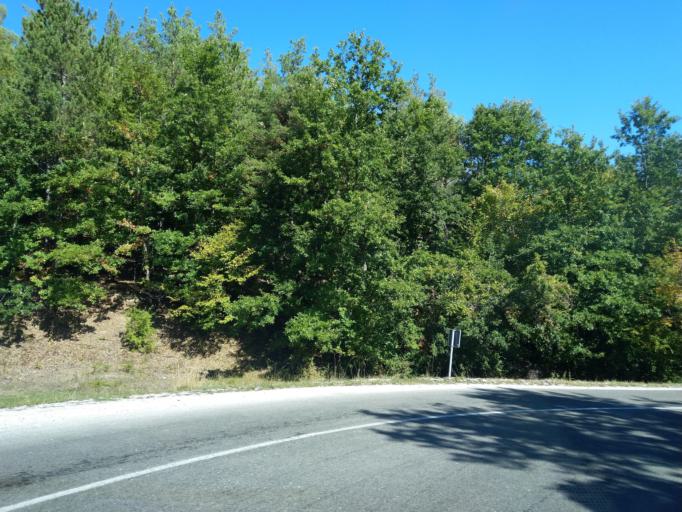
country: RS
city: Sokolovica
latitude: 43.2550
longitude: 20.2482
